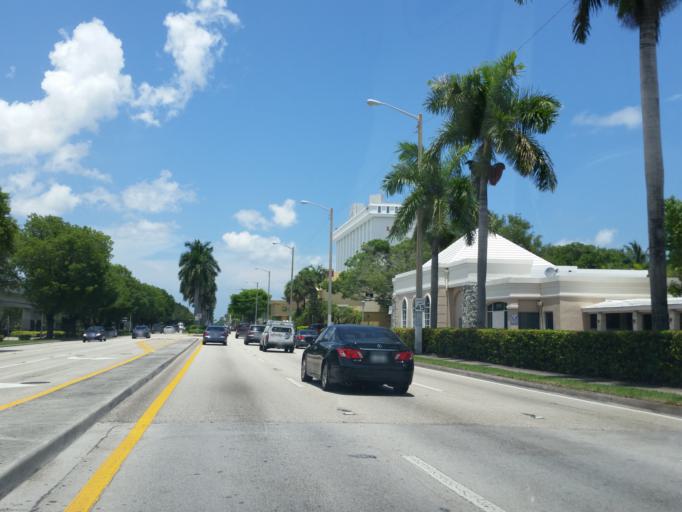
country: US
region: Florida
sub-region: Miami-Dade County
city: South Miami
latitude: 25.7121
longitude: -80.2799
